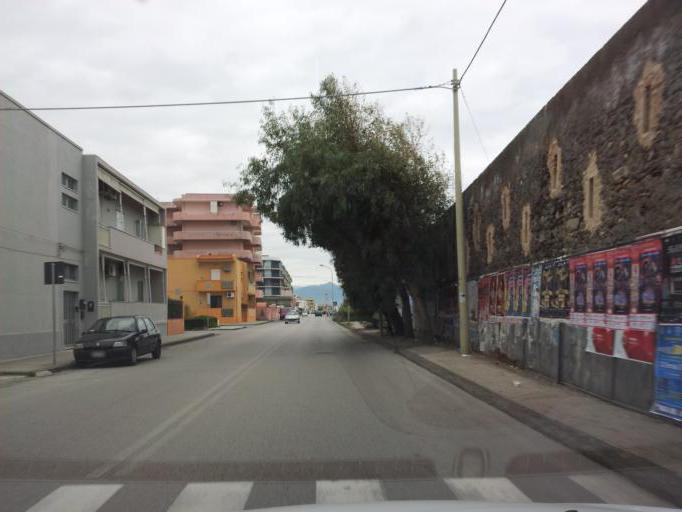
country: IT
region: Sicily
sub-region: Messina
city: Milazzo
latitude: 38.2214
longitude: 15.2342
